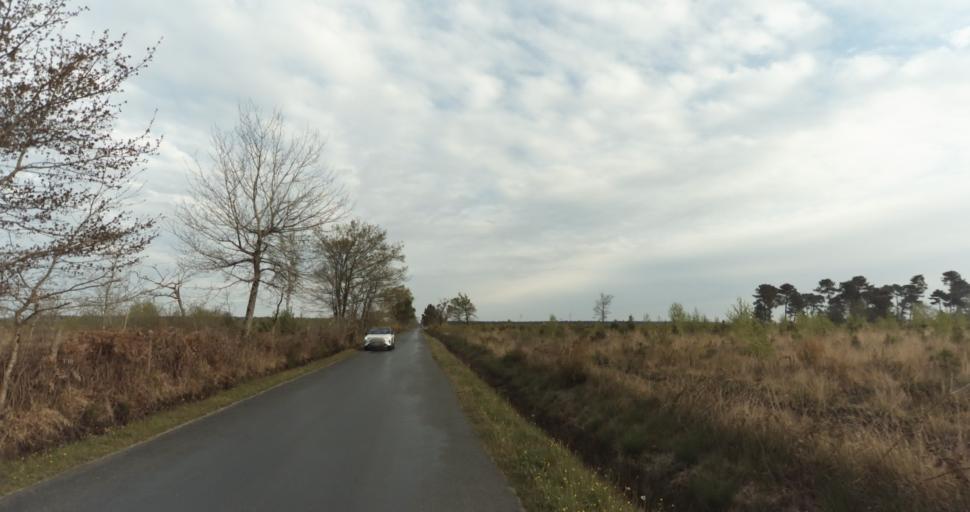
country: FR
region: Aquitaine
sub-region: Departement de la Gironde
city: Saint-Aubin-de-Medoc
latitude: 44.7798
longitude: -0.7450
